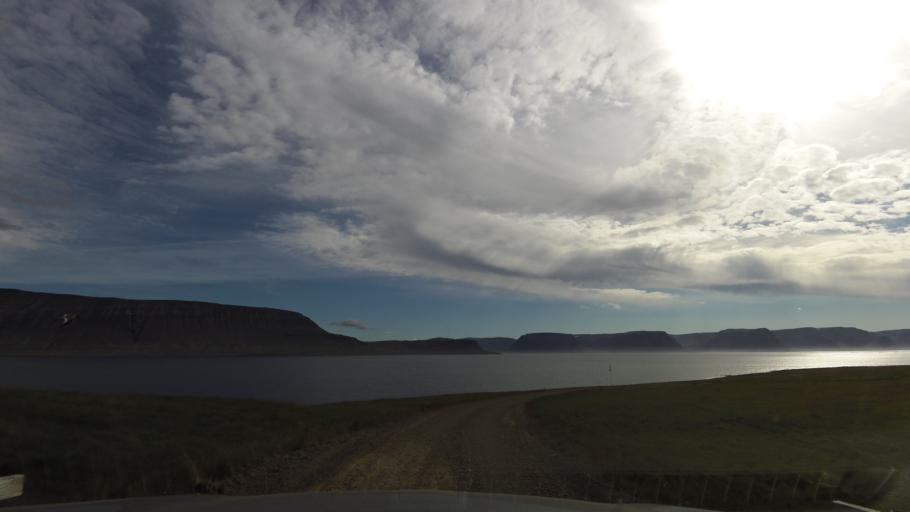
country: IS
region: Westfjords
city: Isafjoerdur
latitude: 65.7586
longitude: -23.4525
